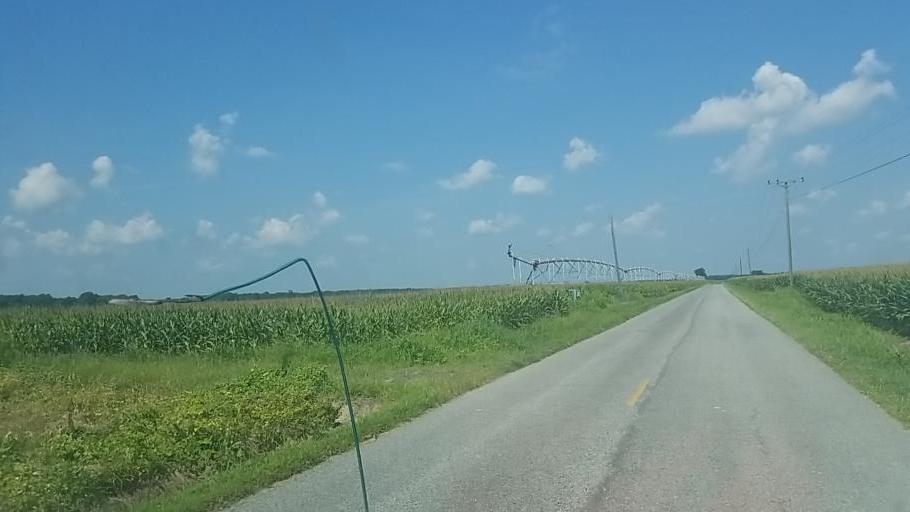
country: US
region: Maryland
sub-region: Worcester County
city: Berlin
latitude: 38.2883
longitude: -75.2398
